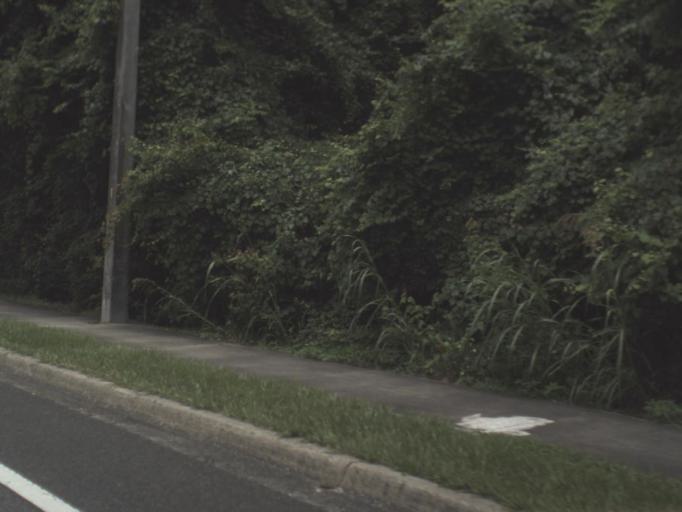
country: US
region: Florida
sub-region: Alachua County
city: Alachua
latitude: 29.6889
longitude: -82.4137
